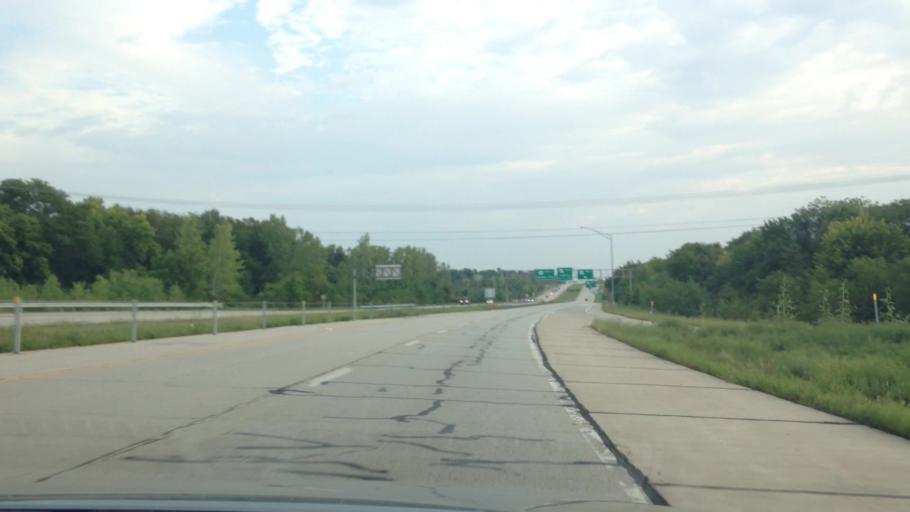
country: US
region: Missouri
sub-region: Clay County
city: Gladstone
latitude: 39.2675
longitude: -94.5851
